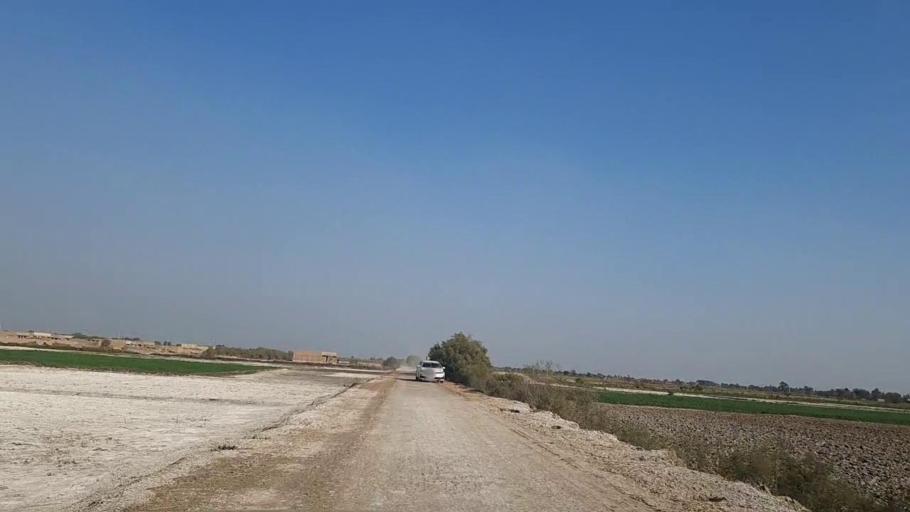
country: PK
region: Sindh
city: Daur
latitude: 26.3178
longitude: 68.1865
